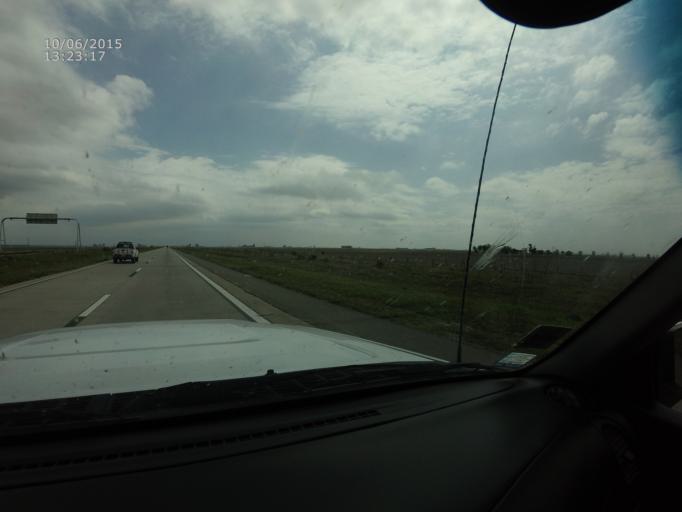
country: AR
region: Cordoba
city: Marcos Juarez
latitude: -32.6614
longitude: -62.1135
